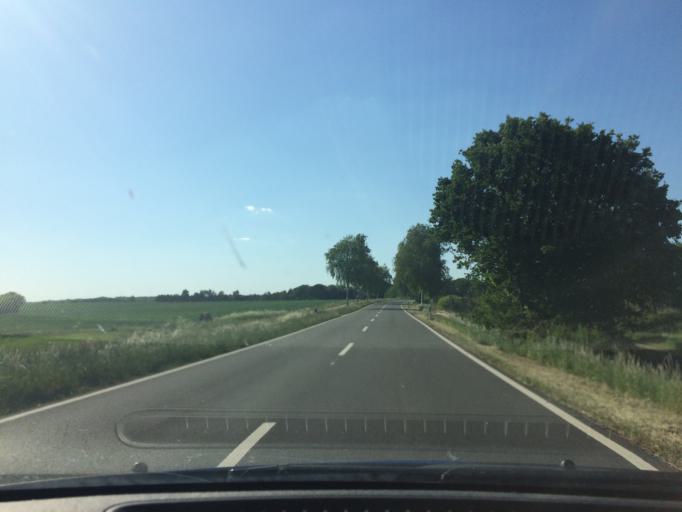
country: DE
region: Lower Saxony
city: Bad Fallingbostel
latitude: 52.9205
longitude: 9.7010
